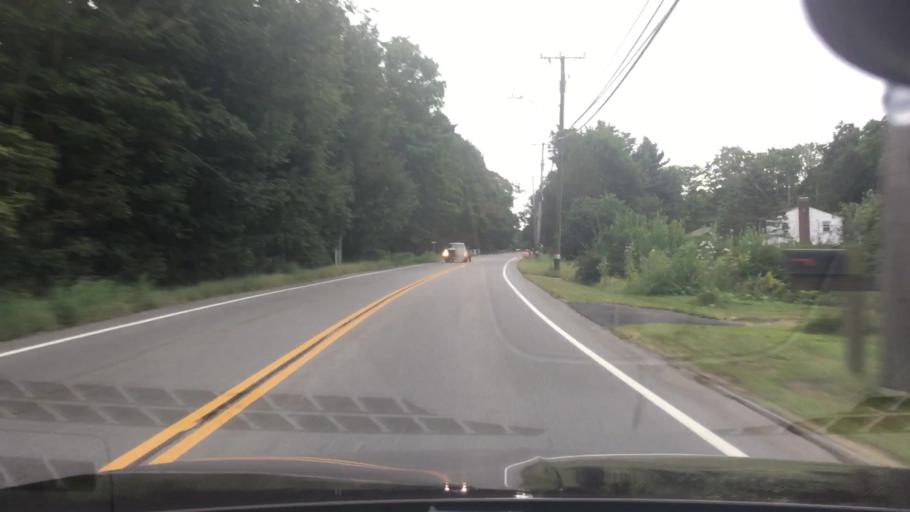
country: US
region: Connecticut
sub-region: New Haven County
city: Madison Center
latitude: 41.3001
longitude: -72.6031
